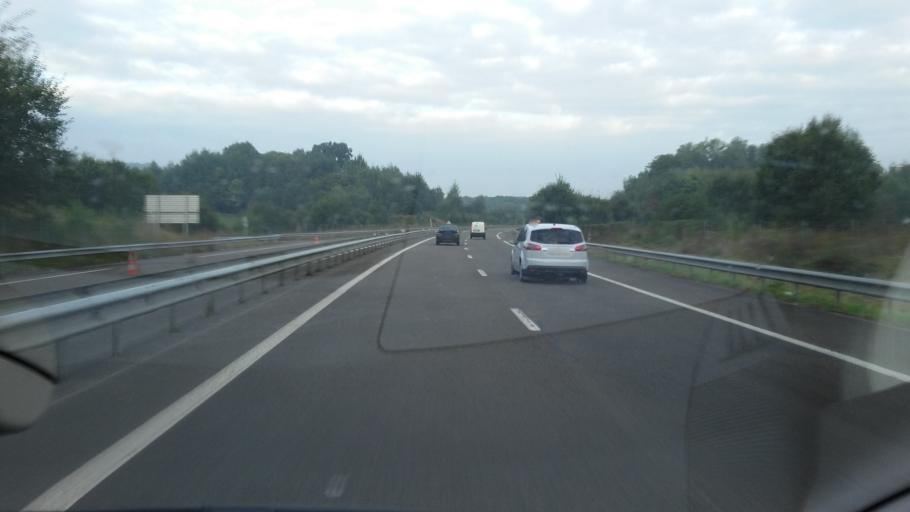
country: FR
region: Champagne-Ardenne
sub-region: Departement des Ardennes
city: La Francheville
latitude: 49.6393
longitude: 4.6097
